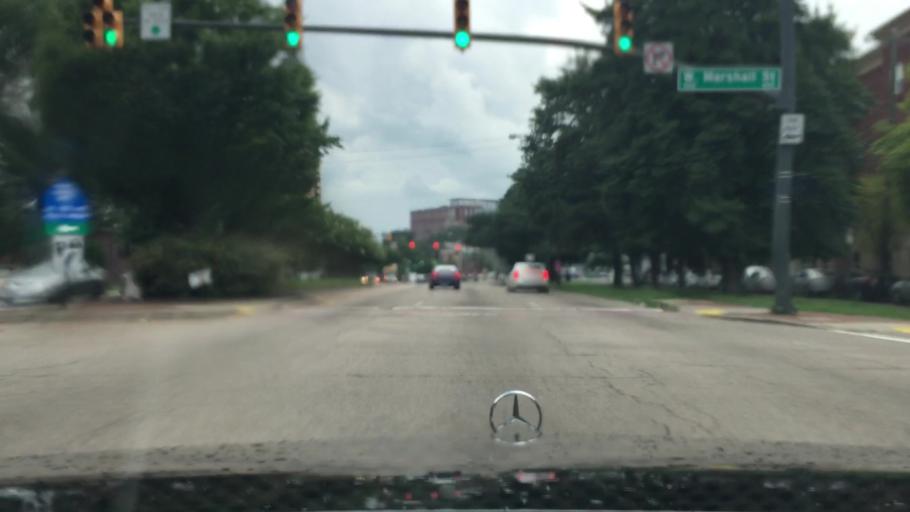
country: US
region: Virginia
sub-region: City of Richmond
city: Richmond
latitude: 37.5497
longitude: -77.4467
